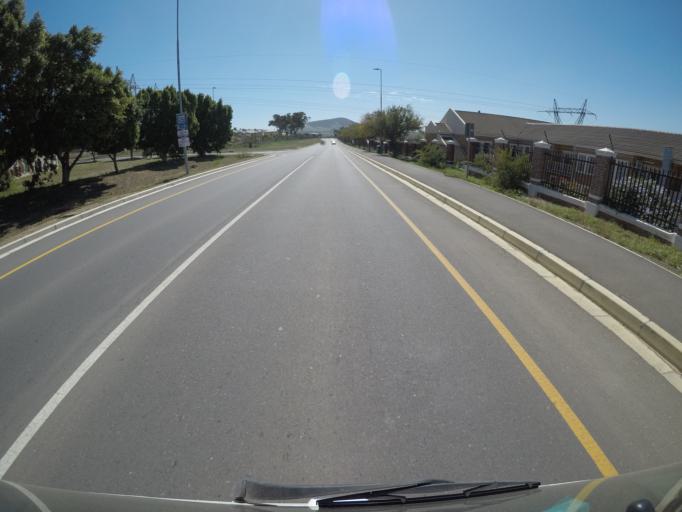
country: ZA
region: Western Cape
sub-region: City of Cape Town
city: Kraaifontein
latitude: -33.8230
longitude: 18.6365
